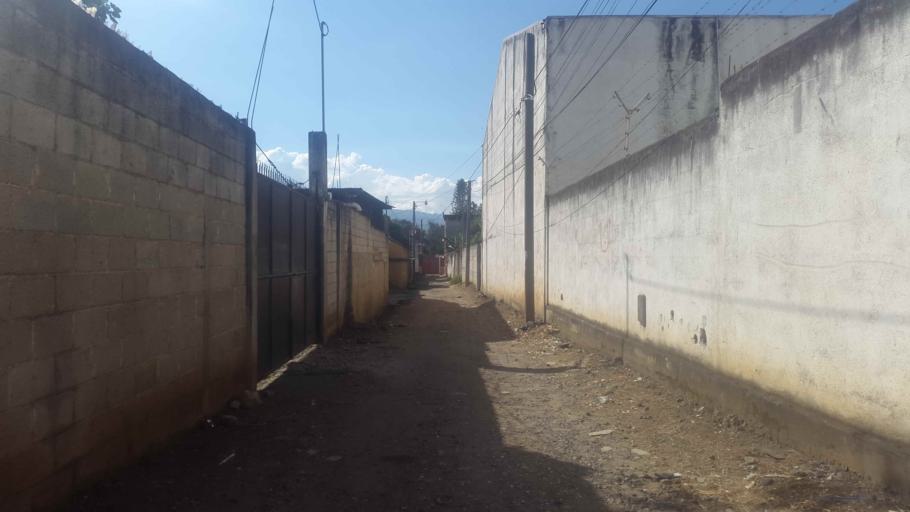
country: GT
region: Guatemala
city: Petapa
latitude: 14.5136
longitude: -90.5417
